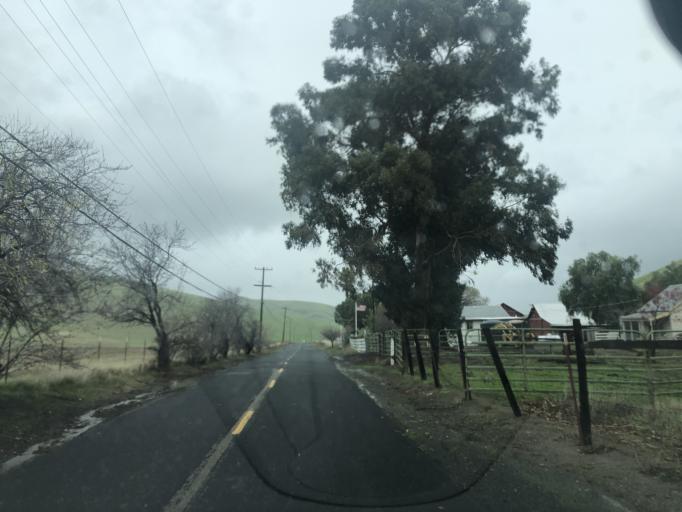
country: US
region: California
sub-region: Contra Costa County
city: Pittsburg
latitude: 37.9782
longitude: -121.8970
